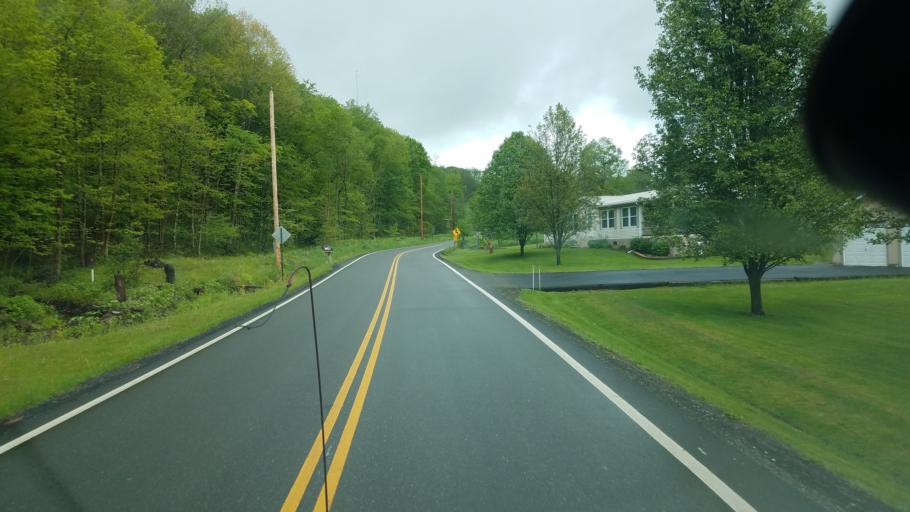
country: US
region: Ohio
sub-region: Harrison County
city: Cadiz
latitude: 40.2721
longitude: -80.8512
